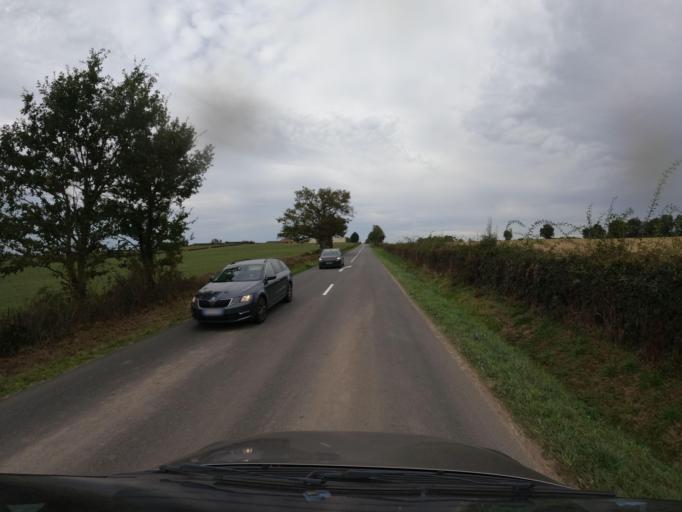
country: FR
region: Poitou-Charentes
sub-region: Departement de la Vienne
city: Saulge
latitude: 46.3801
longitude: 0.8467
